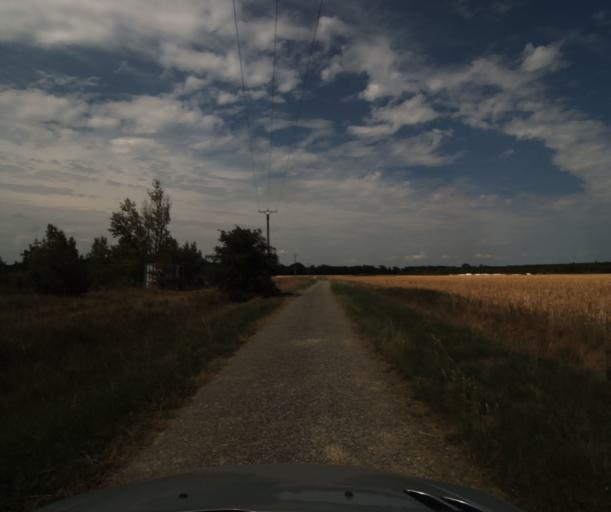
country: FR
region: Midi-Pyrenees
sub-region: Departement de la Haute-Garonne
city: Labastidette
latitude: 43.4863
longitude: 1.2172
